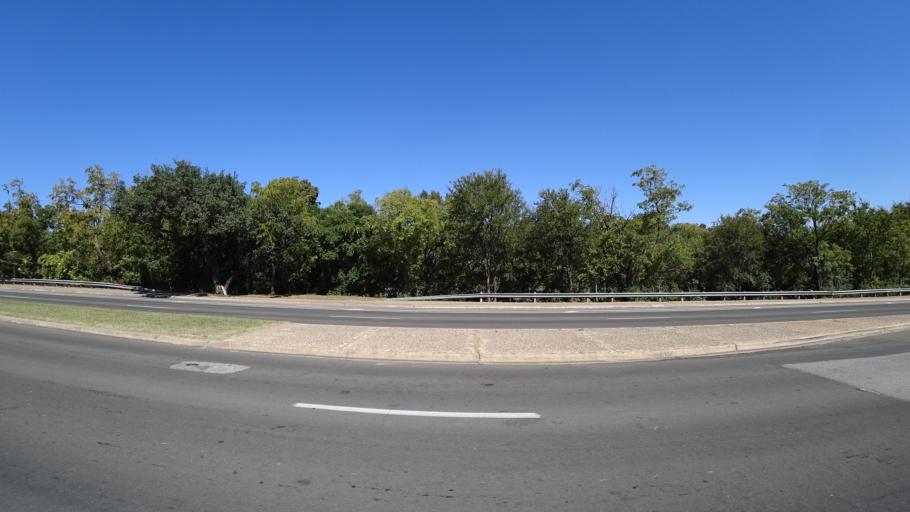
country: US
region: Texas
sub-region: Travis County
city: West Lake Hills
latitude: 30.3622
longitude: -97.7477
